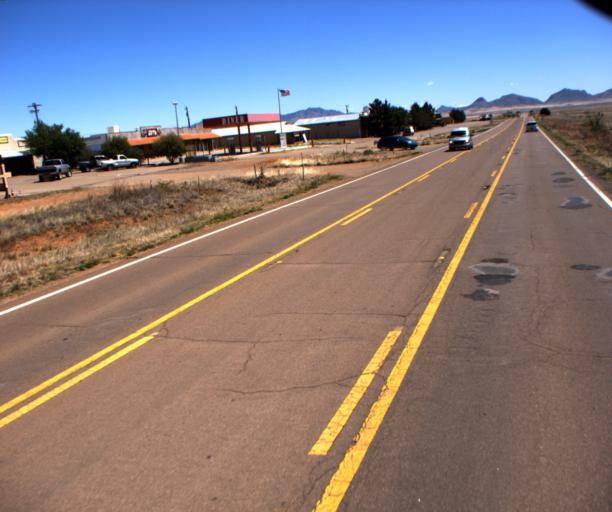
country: US
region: Arizona
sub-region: Pima County
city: Corona de Tucson
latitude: 31.6800
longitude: -110.6506
